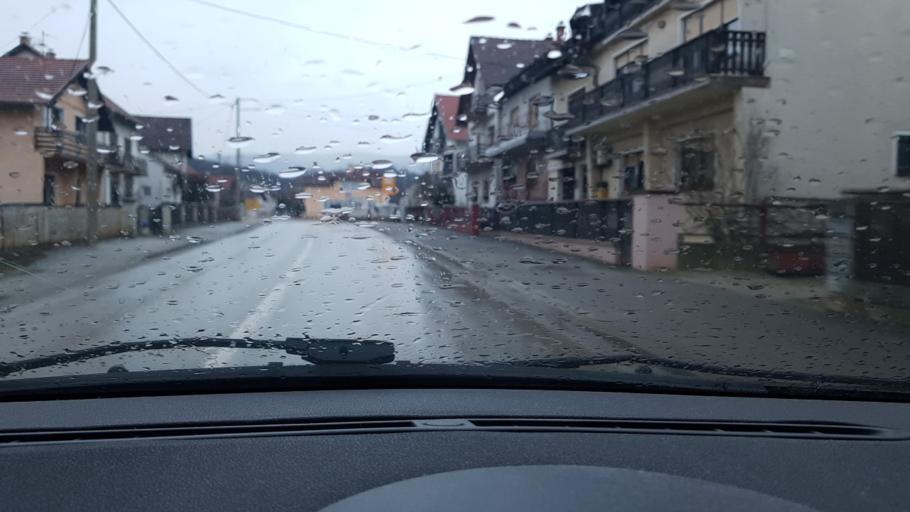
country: HR
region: Krapinsko-Zagorska
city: Oroslavje
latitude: 45.9765
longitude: 15.9229
